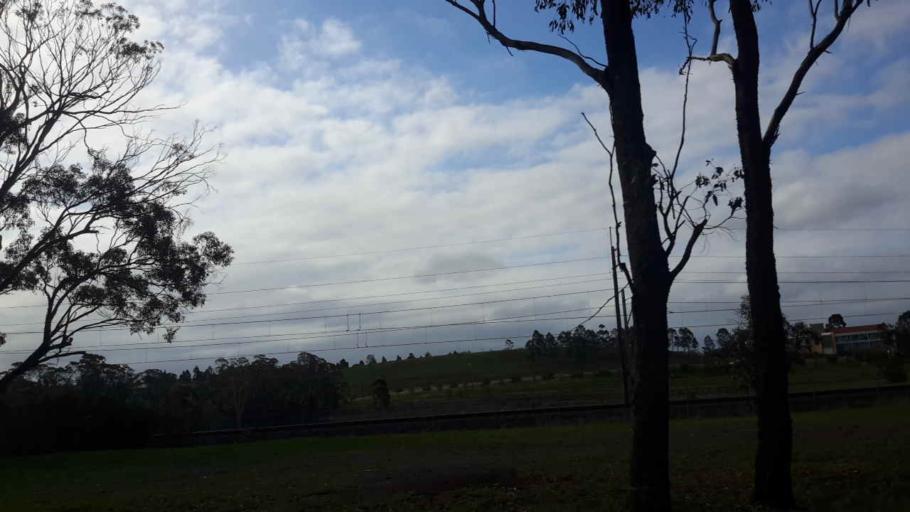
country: AU
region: New South Wales
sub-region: Campbelltown Municipality
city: Glen Alpine
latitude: -34.0740
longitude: 150.7902
